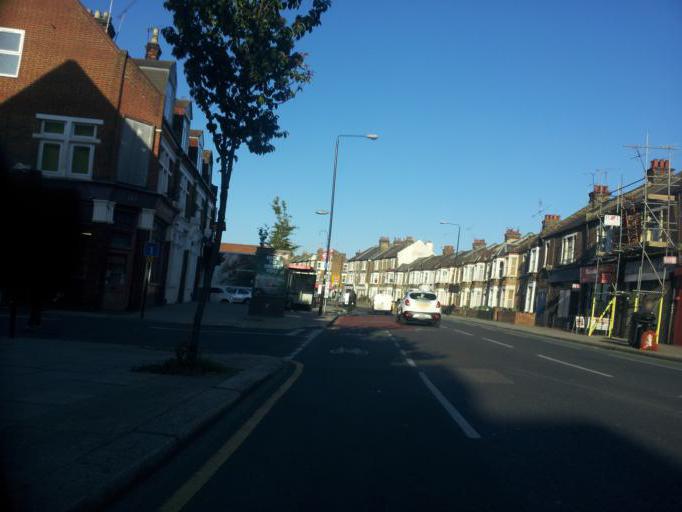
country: GB
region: England
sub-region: Greater London
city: Blackheath
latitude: 51.4861
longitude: 0.0132
